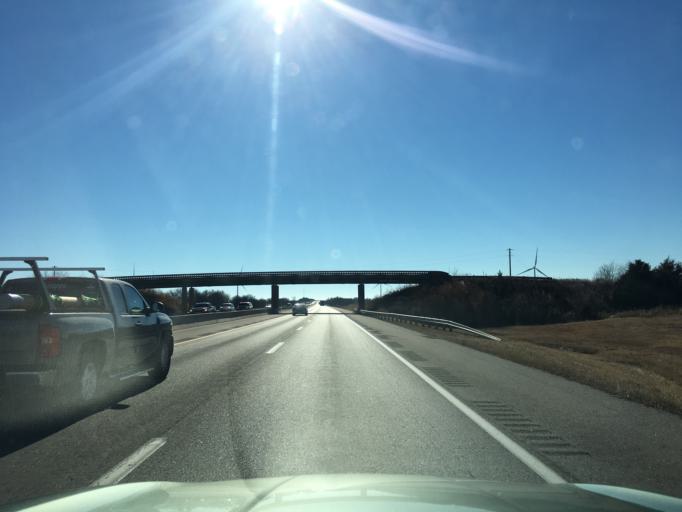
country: US
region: Kansas
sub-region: Sumner County
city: Wellington
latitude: 37.1461
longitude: -97.3395
